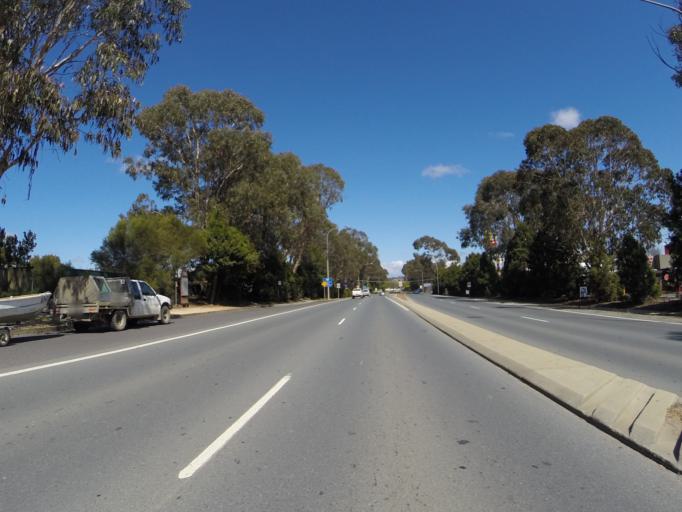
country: AU
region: New South Wales
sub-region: Queanbeyan
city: Queanbeyan
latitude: -35.3492
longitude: 149.2433
